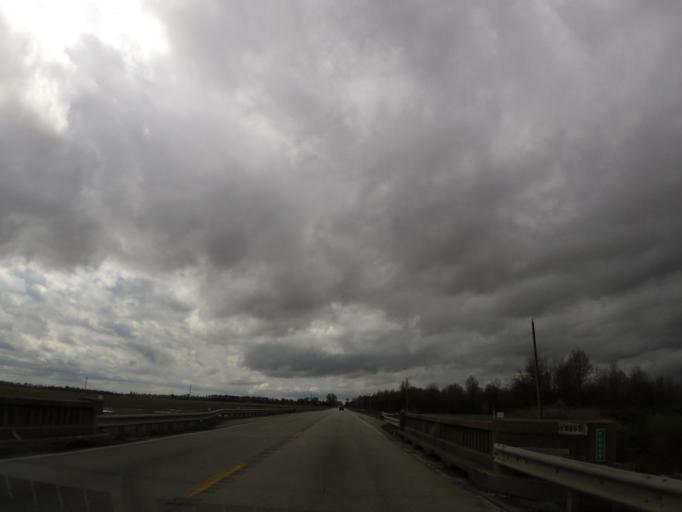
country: US
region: Missouri
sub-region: Butler County
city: Poplar Bluff
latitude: 36.6085
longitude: -90.5205
